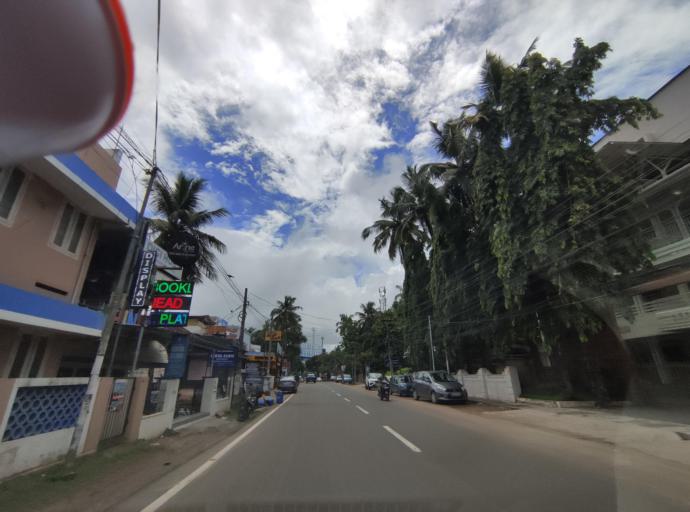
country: IN
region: Kerala
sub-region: Thiruvananthapuram
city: Thiruvananthapuram
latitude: 8.4992
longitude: 76.9600
